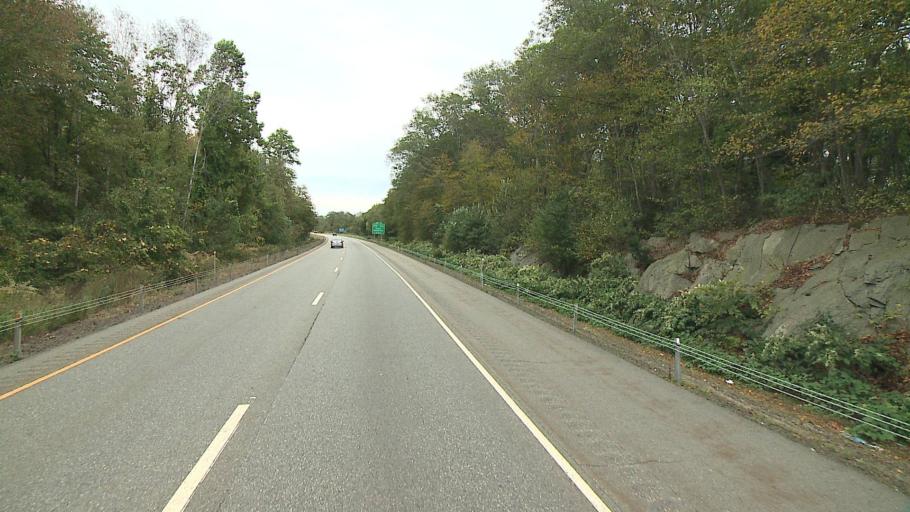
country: US
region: Connecticut
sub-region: Middlesex County
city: Essex Village
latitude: 41.3567
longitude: -72.4161
